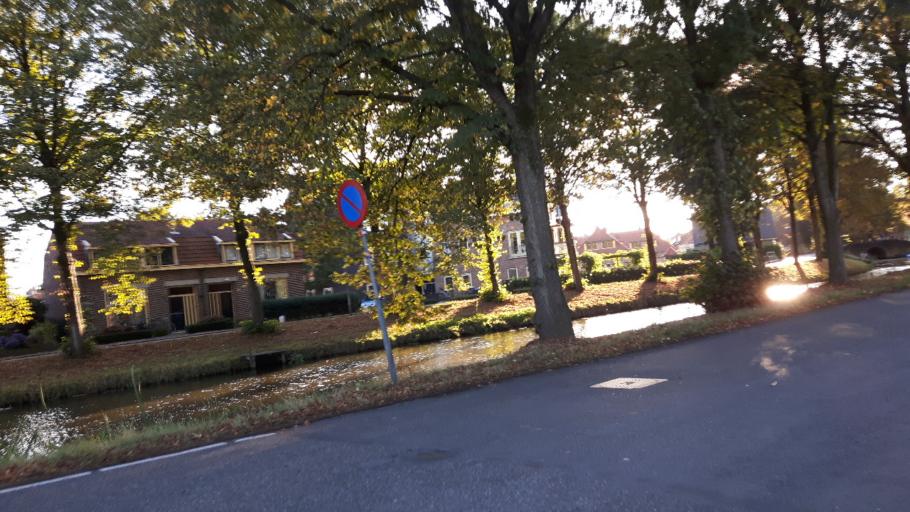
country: NL
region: Utrecht
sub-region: Gemeente Oudewater
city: Oudewater
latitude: 52.0258
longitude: 4.8734
